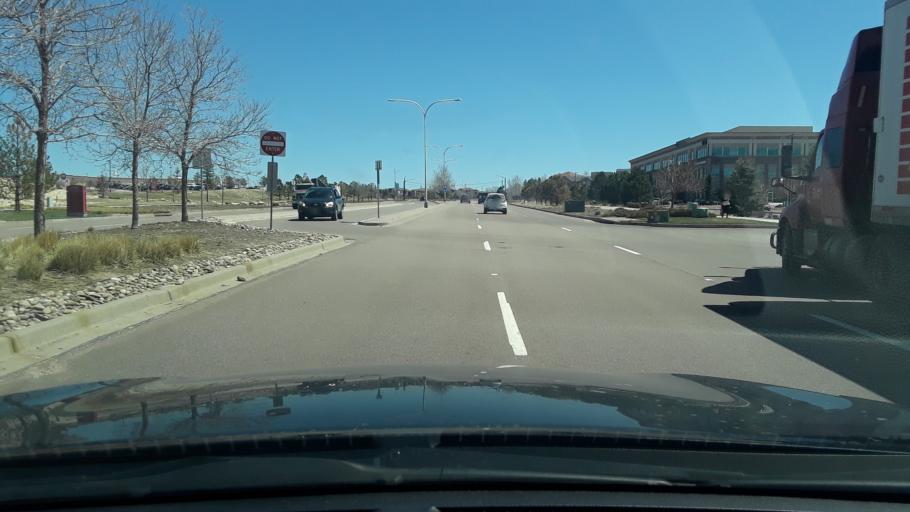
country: US
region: Colorado
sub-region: El Paso County
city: Black Forest
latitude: 38.9658
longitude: -104.7552
